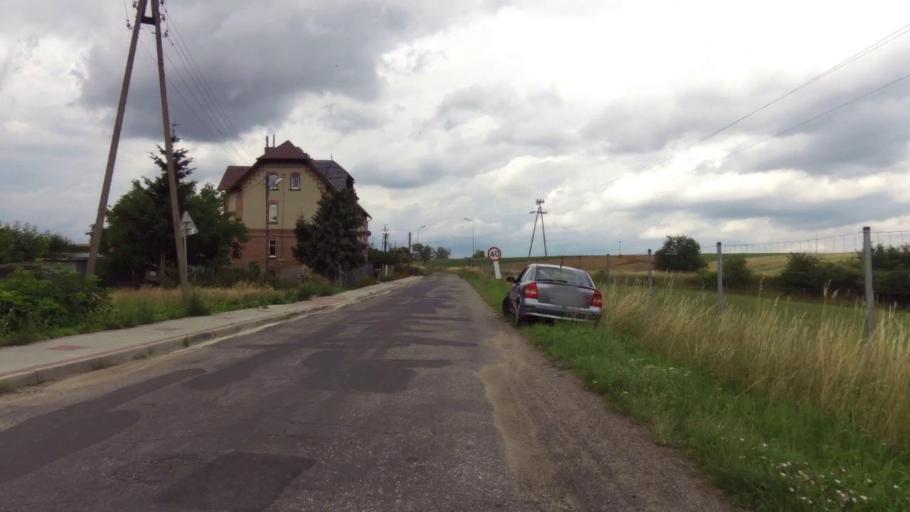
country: PL
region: West Pomeranian Voivodeship
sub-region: Powiat gryfinski
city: Moryn
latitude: 52.8731
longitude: 14.3908
